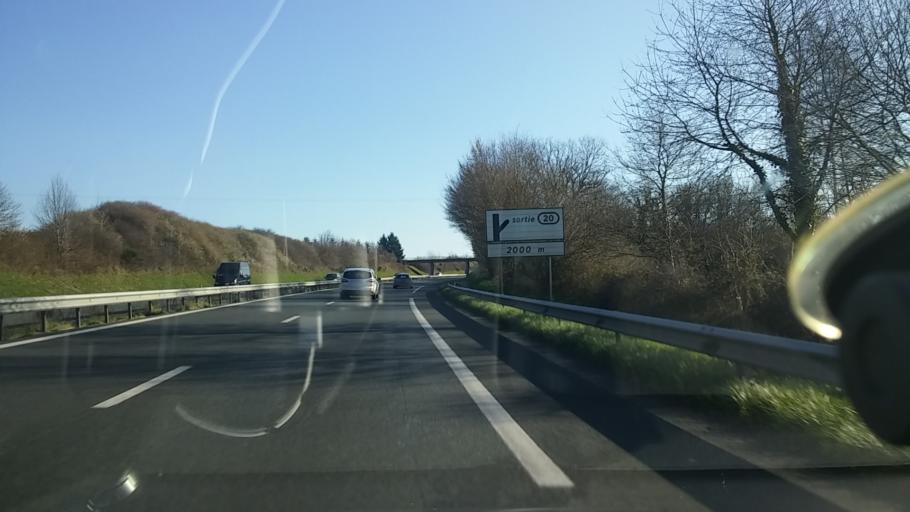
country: FR
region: Centre
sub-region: Departement de l'Indre
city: Chantome
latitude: 46.4603
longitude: 1.4992
